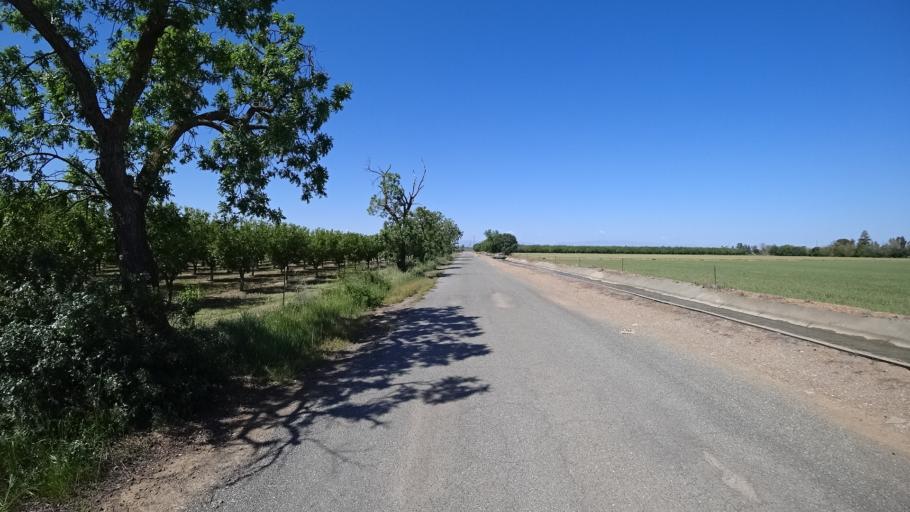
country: US
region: California
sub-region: Glenn County
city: Orland
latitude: 39.7653
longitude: -122.1772
